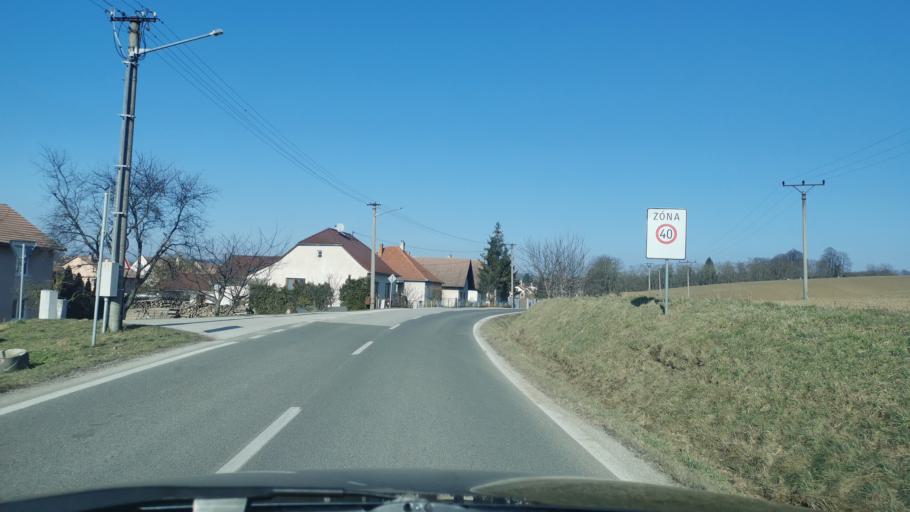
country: SK
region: Trnavsky
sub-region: Okres Senica
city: Senica
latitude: 48.6860
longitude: 17.3970
